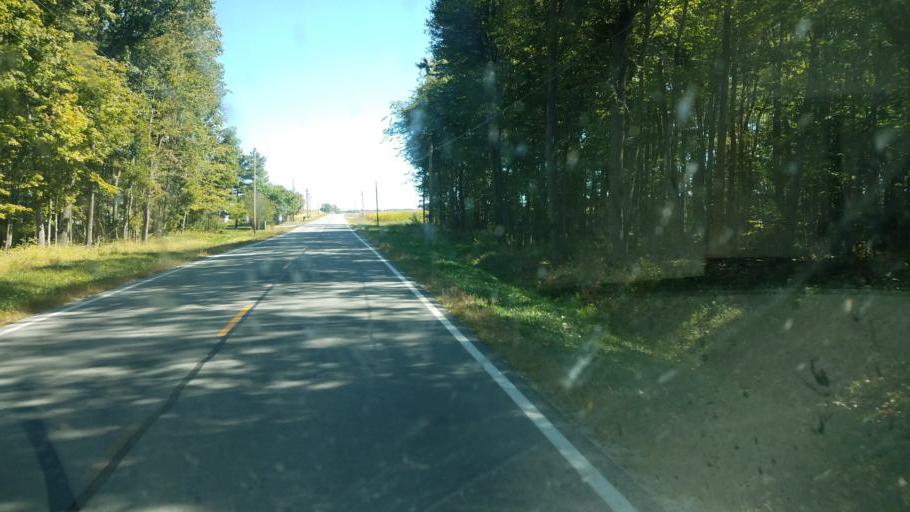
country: US
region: Ohio
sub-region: Crawford County
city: Bucyrus
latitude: 40.9504
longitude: -82.9812
